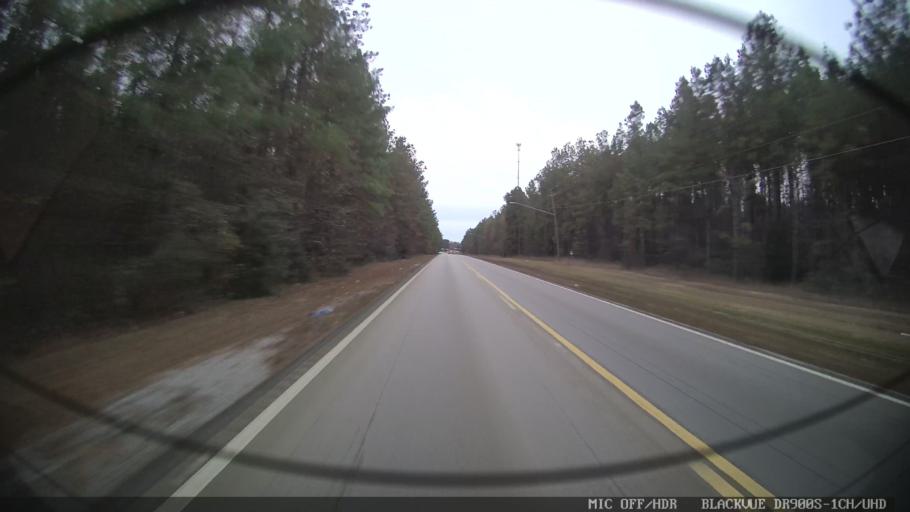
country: US
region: Mississippi
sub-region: Clarke County
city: Stonewall
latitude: 32.0530
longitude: -88.8976
